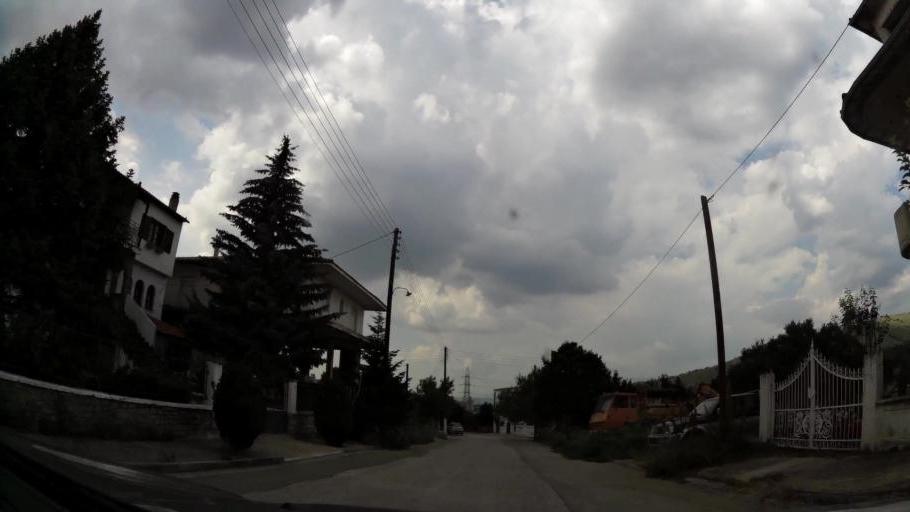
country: GR
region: West Macedonia
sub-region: Nomos Kozanis
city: Koila
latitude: 40.3298
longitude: 21.8252
